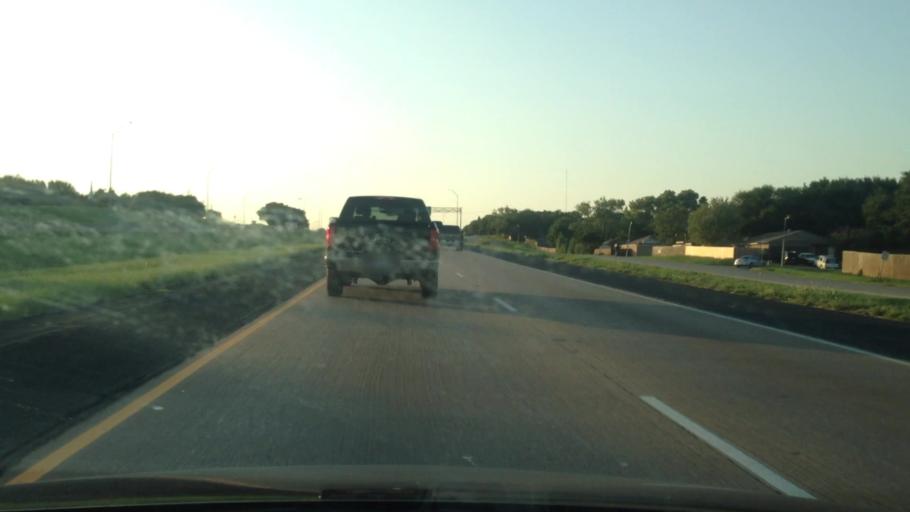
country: US
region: Texas
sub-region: Tarrant County
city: Kennedale
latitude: 32.6619
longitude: -97.1981
